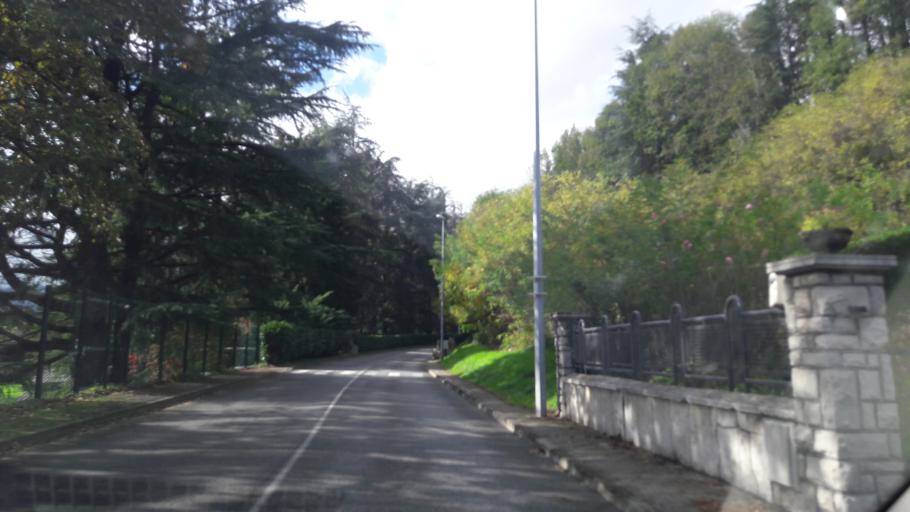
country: FR
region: Rhone-Alpes
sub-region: Departement de la Savoie
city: Montmelian
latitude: 45.4979
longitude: 6.0543
